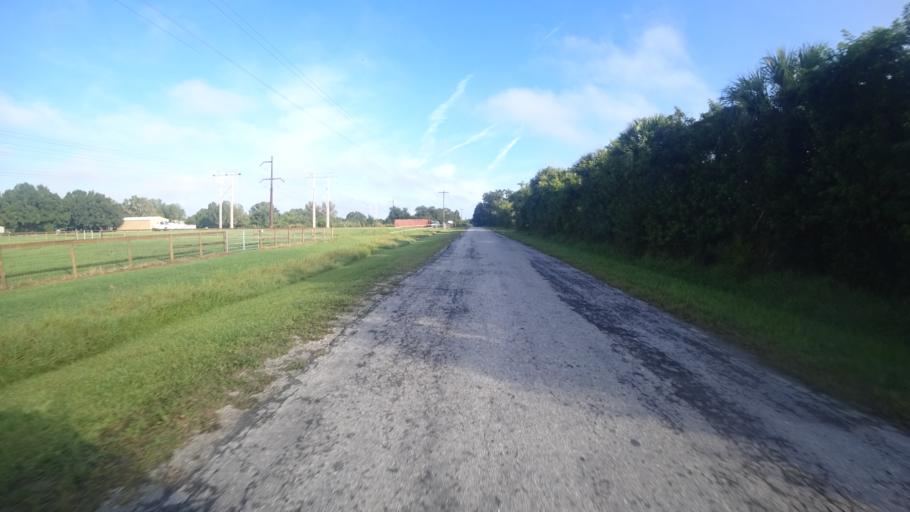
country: US
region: Florida
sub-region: Manatee County
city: Ellenton
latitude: 27.5367
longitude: -82.4582
